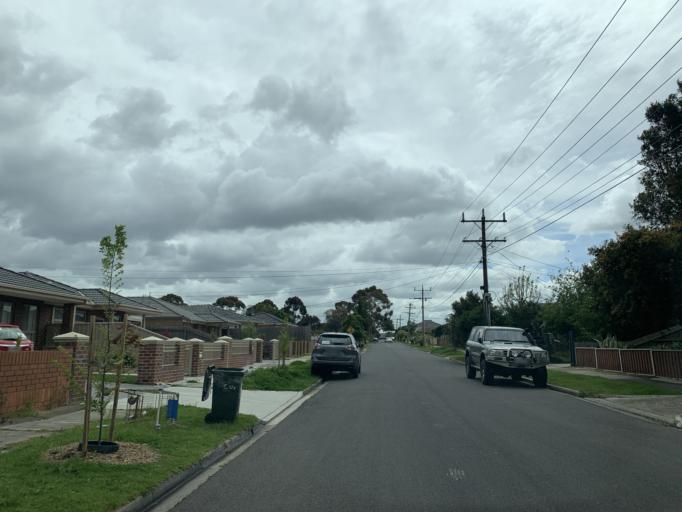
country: AU
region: Victoria
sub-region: Brimbank
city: Kealba
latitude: -37.7444
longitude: 144.8218
